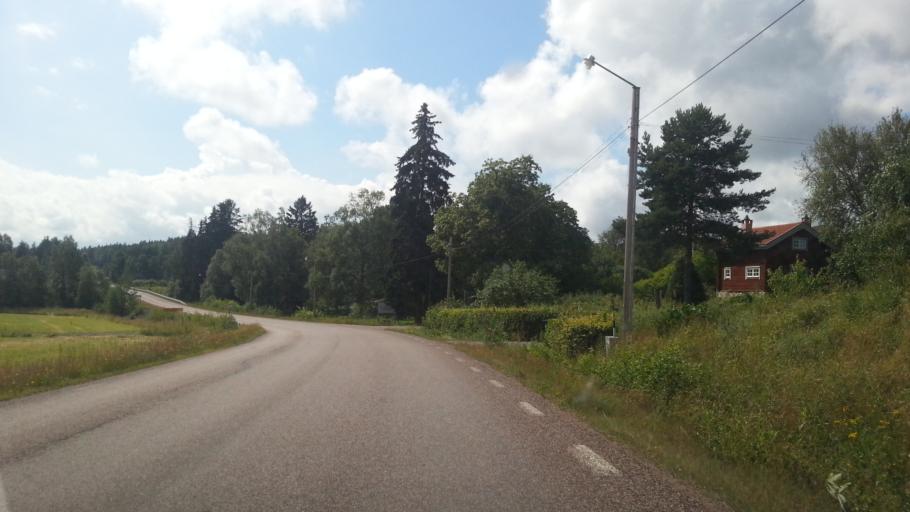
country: SE
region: Dalarna
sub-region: Faluns Kommun
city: Falun
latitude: 60.6338
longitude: 15.7692
